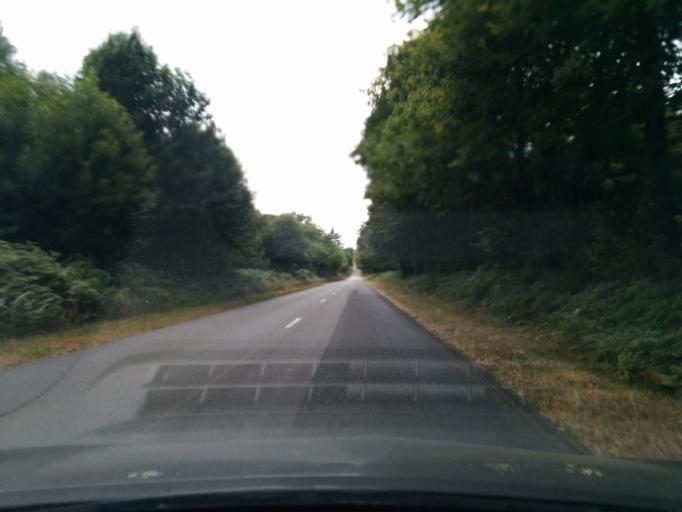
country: FR
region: Centre
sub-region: Departement du Cher
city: Neuvy-sur-Barangeon
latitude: 47.3250
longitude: 2.3260
